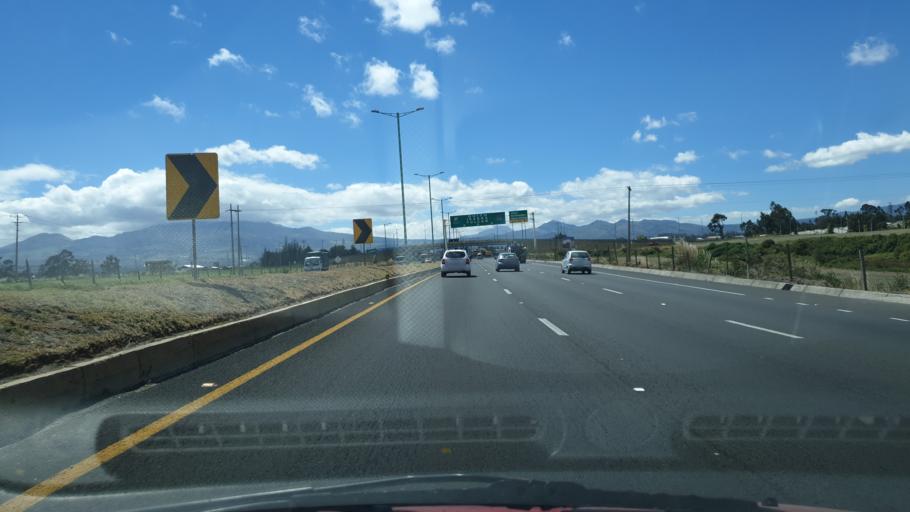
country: EC
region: Cotopaxi
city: Saquisili
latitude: -0.8180
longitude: -78.6244
